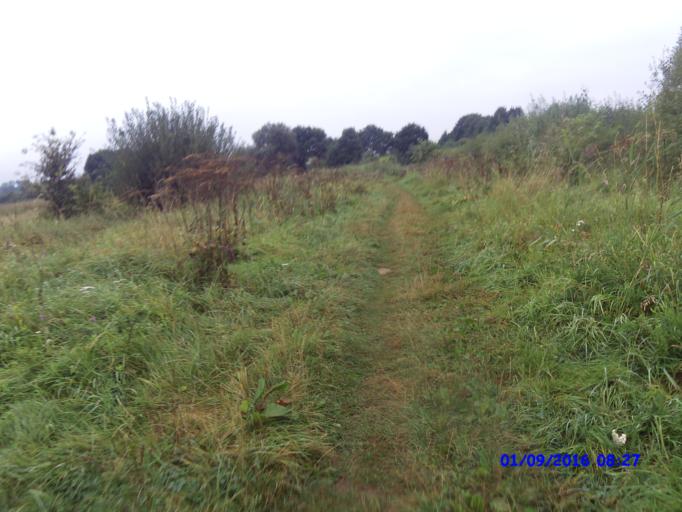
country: BE
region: Flanders
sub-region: Provincie Antwerpen
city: Bonheiden
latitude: 51.0252
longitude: 4.5148
